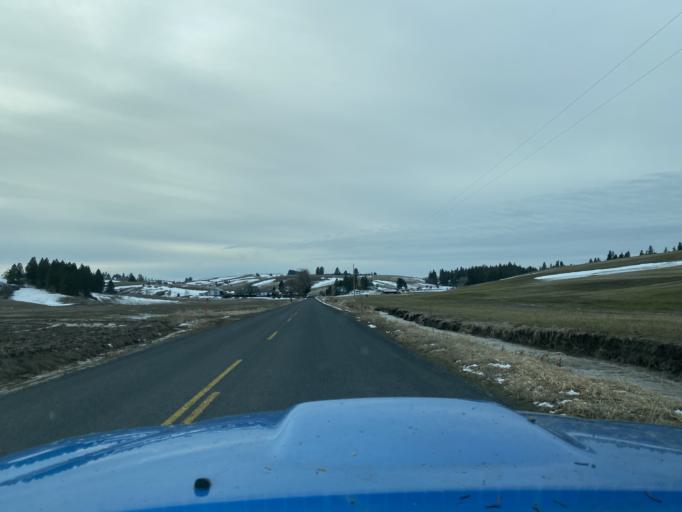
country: US
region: Idaho
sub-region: Latah County
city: Moscow
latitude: 46.6869
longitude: -116.8985
